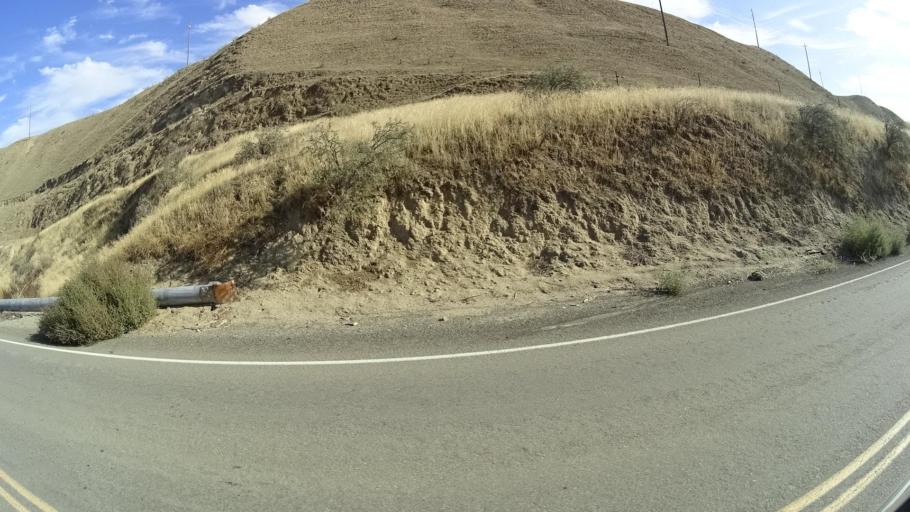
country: US
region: California
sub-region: Kern County
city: Oildale
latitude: 35.5374
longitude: -118.9589
